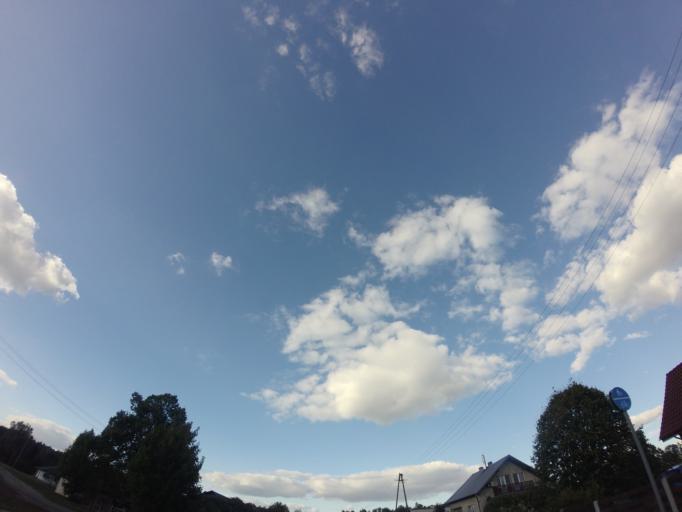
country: PL
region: Greater Poland Voivodeship
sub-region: Powiat nowotomyski
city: Nowy Tomysl
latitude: 52.2724
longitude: 16.1273
